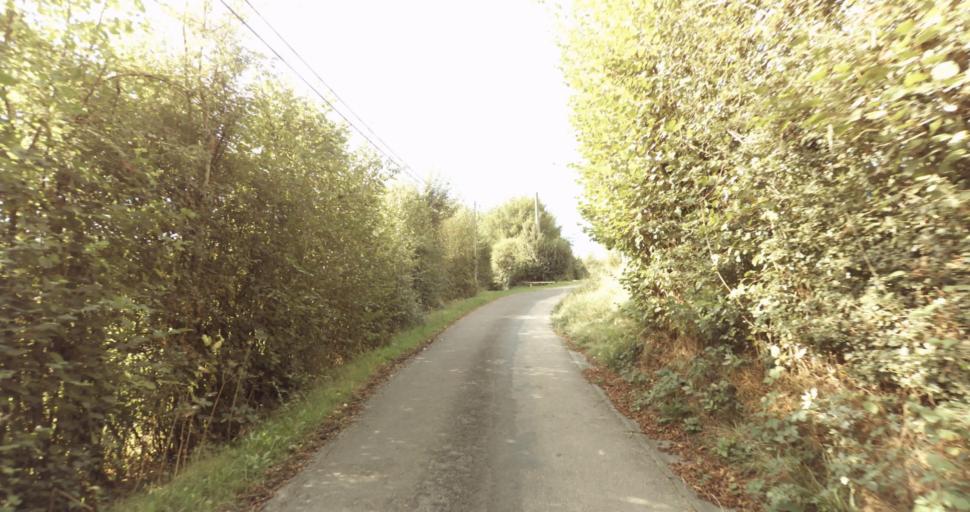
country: FR
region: Lower Normandy
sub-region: Departement de l'Orne
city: Gace
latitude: 48.8284
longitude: 0.2202
